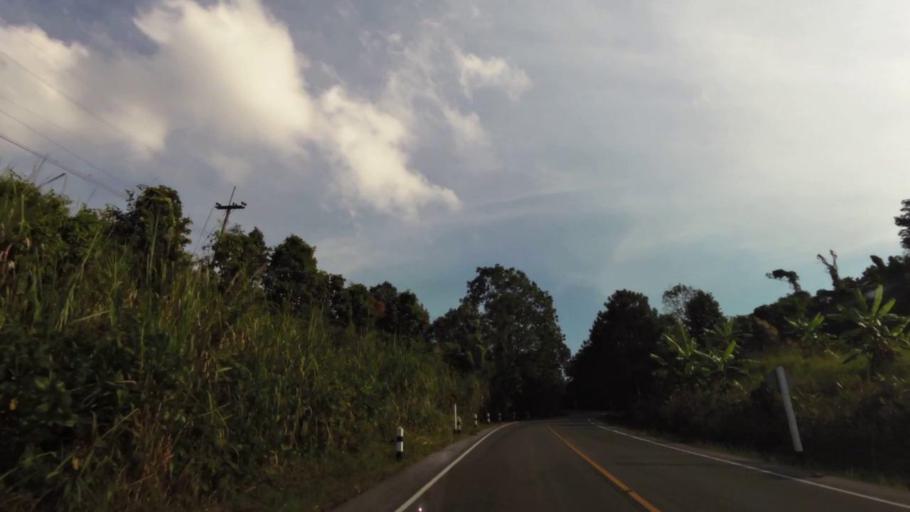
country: TH
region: Chiang Rai
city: Khun Tan
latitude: 19.8725
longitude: 100.3215
